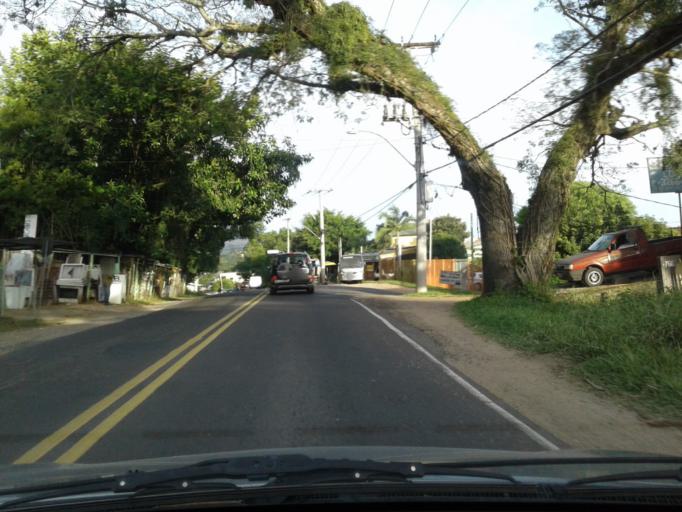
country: BR
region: Rio Grande do Sul
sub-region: Porto Alegre
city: Porto Alegre
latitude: -30.1109
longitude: -51.2187
